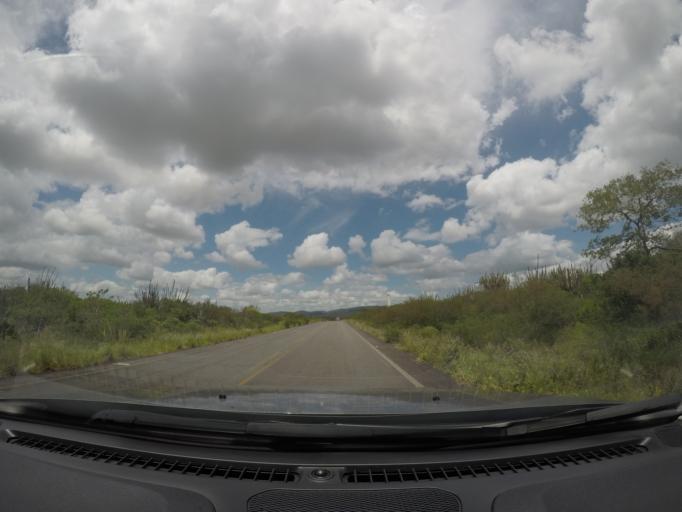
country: BR
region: Bahia
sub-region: Ipira
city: Ipira
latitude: -12.1914
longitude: -39.7675
